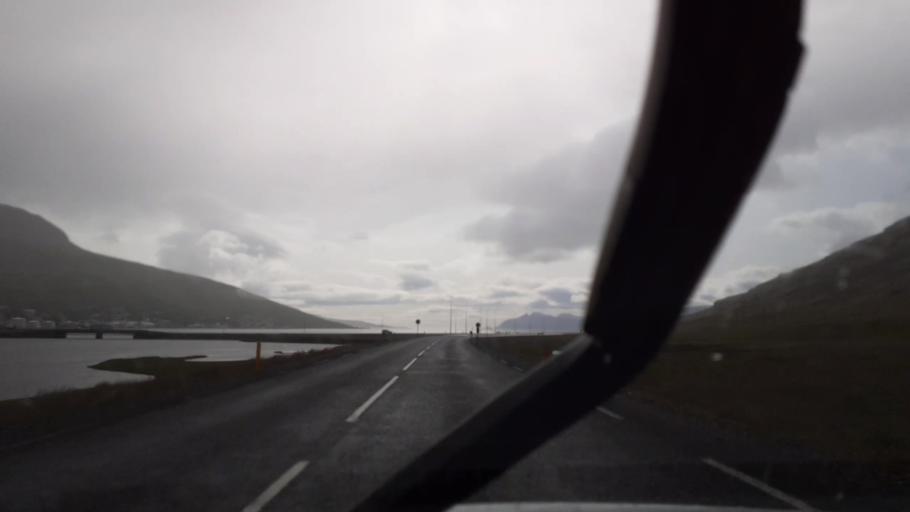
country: IS
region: East
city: Eskifjoerdur
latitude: 65.0755
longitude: -14.0469
